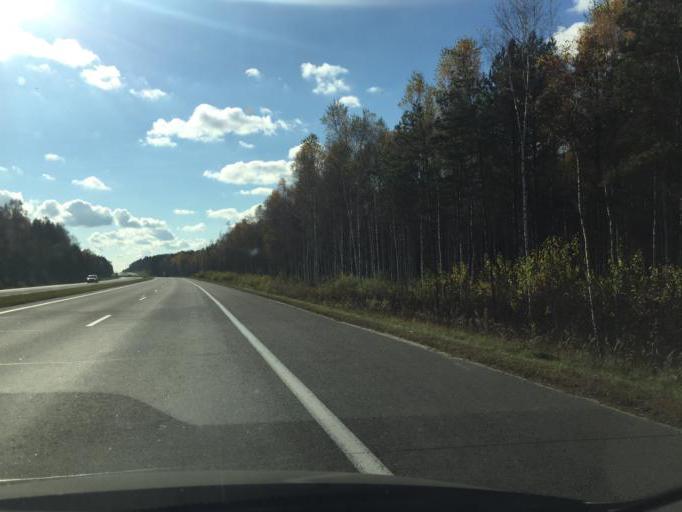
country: BY
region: Minsk
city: Slabada
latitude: 53.9369
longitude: 27.9631
